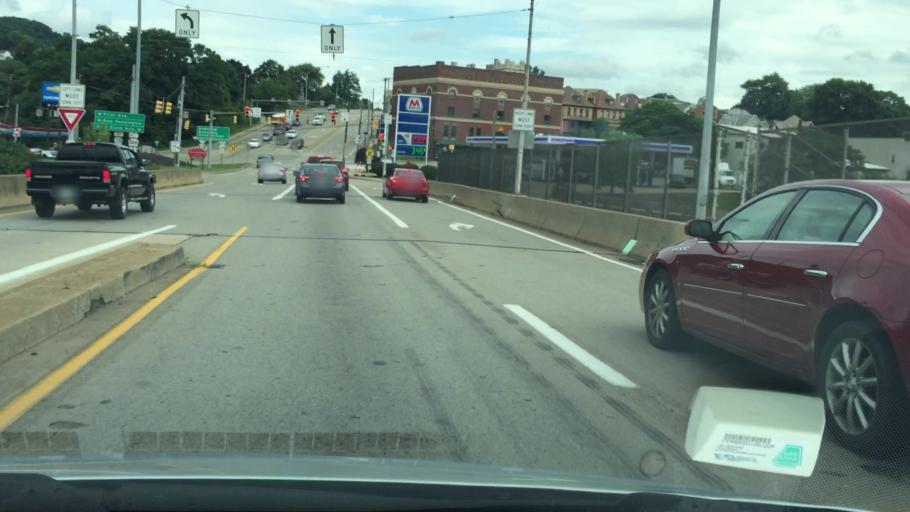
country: US
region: Pennsylvania
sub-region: Allegheny County
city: Tarentum
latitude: 40.6006
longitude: -79.7568
